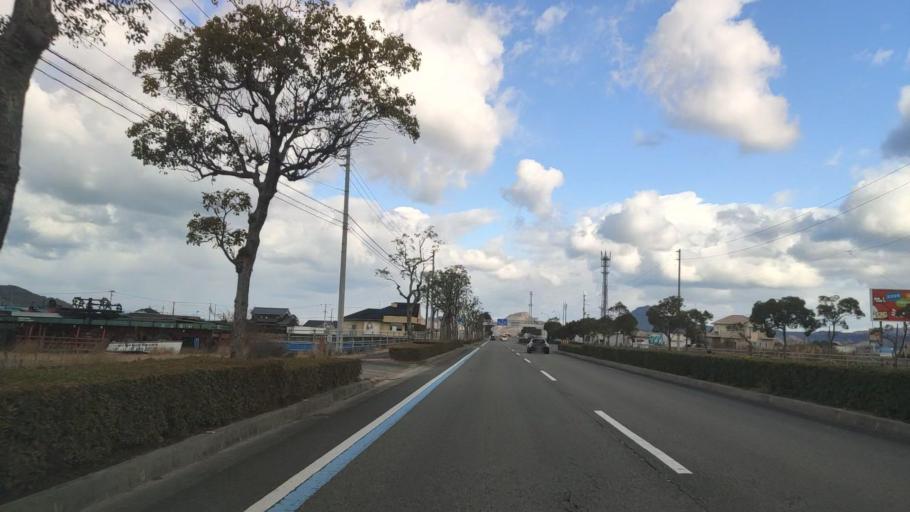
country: JP
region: Ehime
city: Hojo
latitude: 33.9513
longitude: 132.7746
